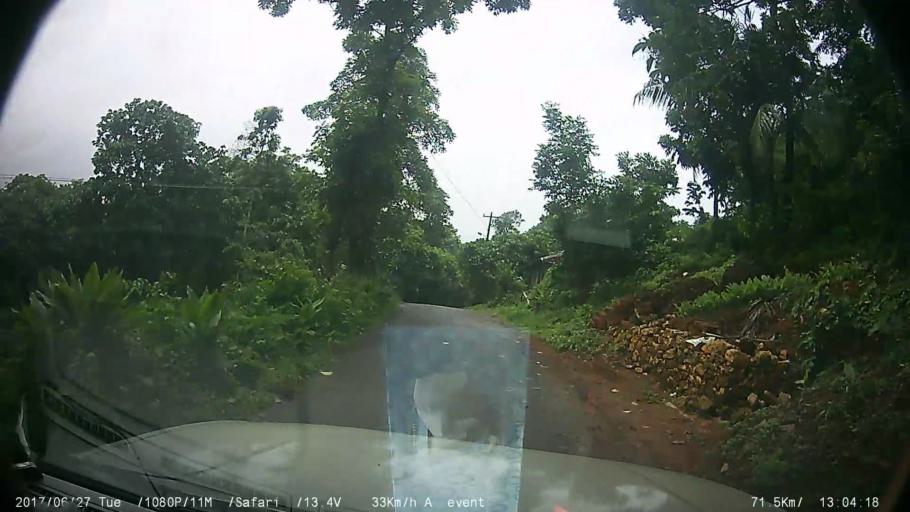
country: IN
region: Kerala
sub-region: Kottayam
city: Palackattumala
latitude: 9.7847
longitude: 76.5455
